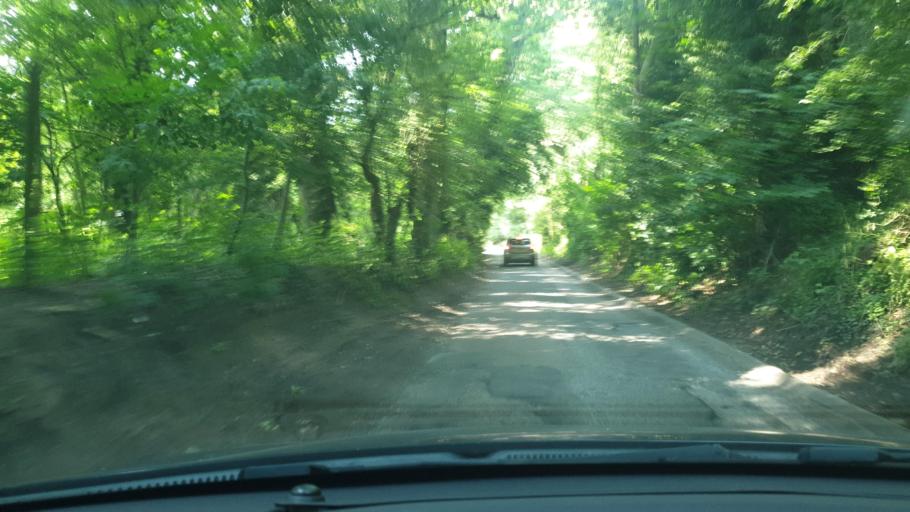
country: GB
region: England
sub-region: Suffolk
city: East Bergholt
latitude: 51.9450
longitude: 1.0243
